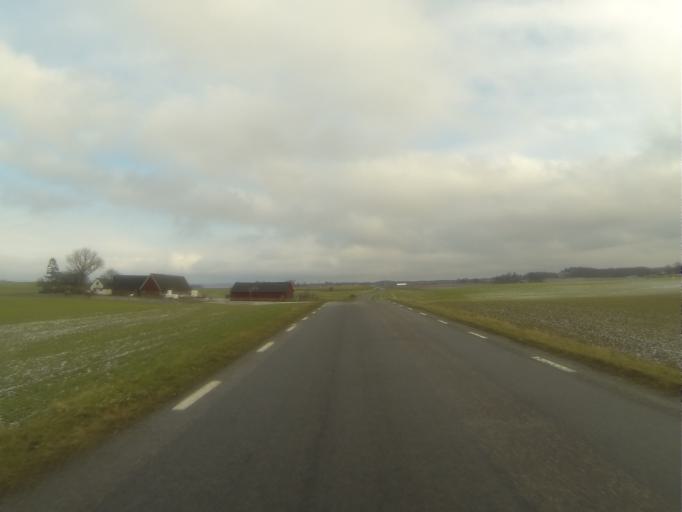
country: SE
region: Skane
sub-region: Svedala Kommun
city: Klagerup
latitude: 55.5935
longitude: 13.3063
